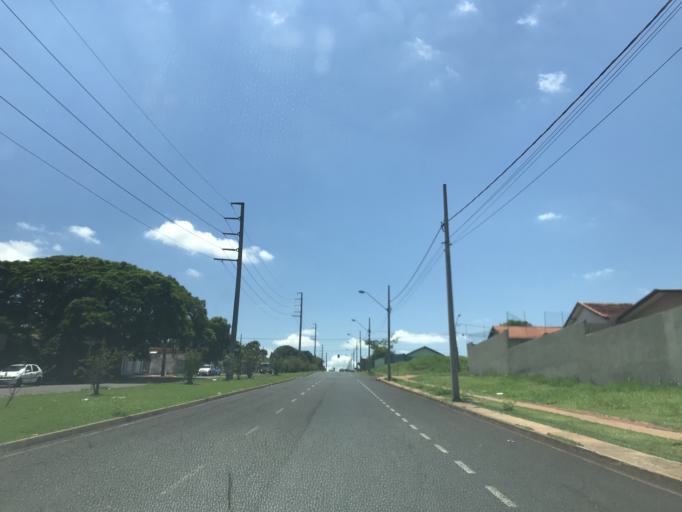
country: BR
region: Parana
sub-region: Maringa
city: Maringa
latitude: -23.4571
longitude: -51.9263
